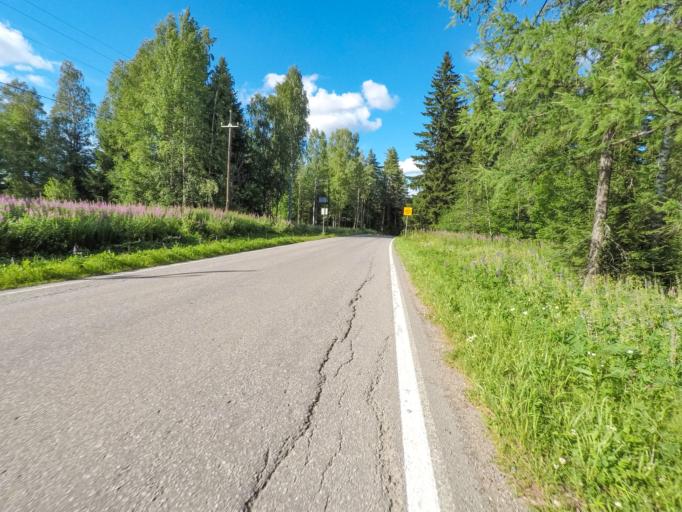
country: FI
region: South Karelia
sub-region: Imatra
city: Imatra
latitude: 61.1431
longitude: 28.7448
